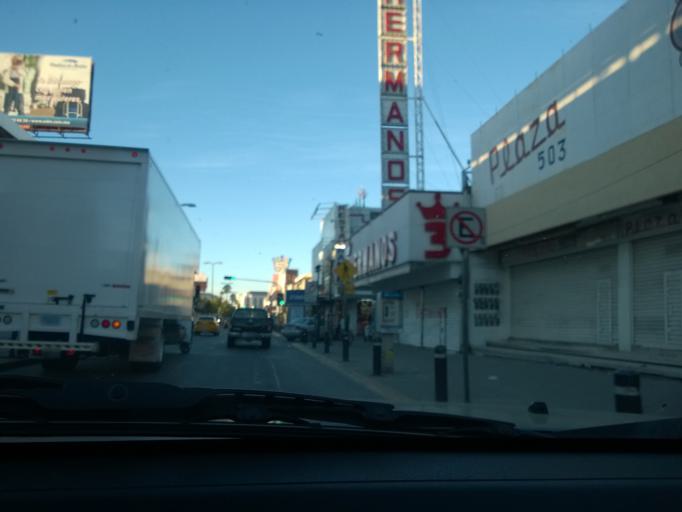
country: MX
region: Guanajuato
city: Leon
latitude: 21.1218
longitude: -101.6621
